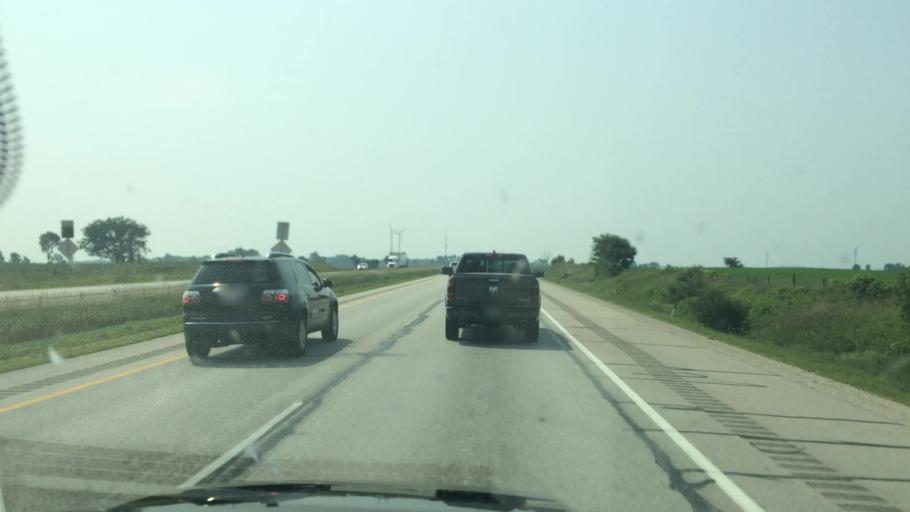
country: US
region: Wisconsin
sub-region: Dodge County
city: Lomira
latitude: 43.6742
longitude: -88.4420
